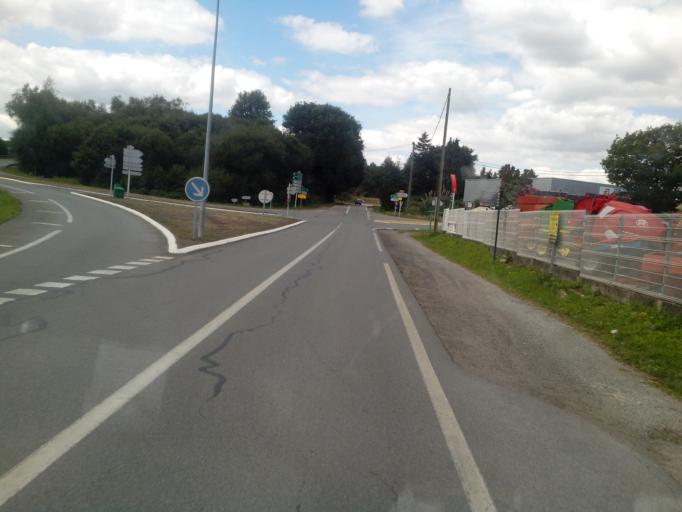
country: FR
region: Brittany
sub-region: Departement du Morbihan
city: Guegon
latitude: 47.9552
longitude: -2.5663
